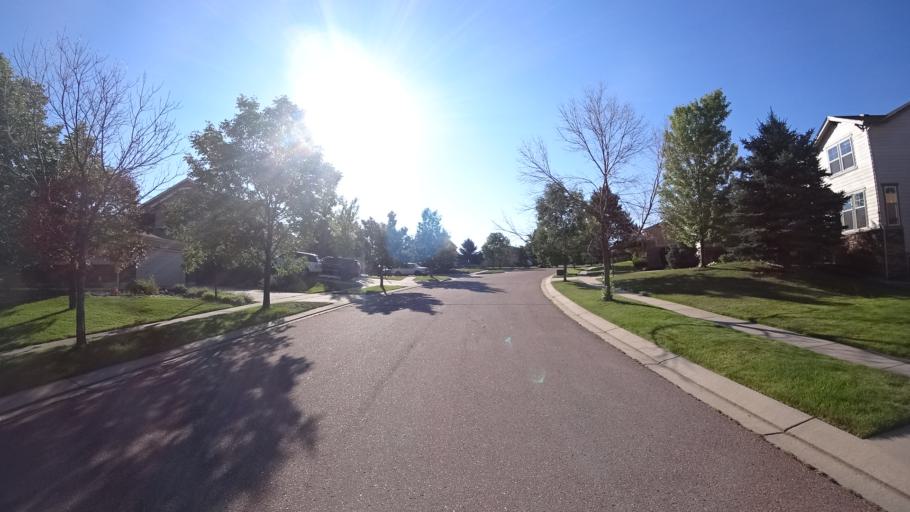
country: US
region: Colorado
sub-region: El Paso County
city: Black Forest
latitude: 38.9815
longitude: -104.7725
